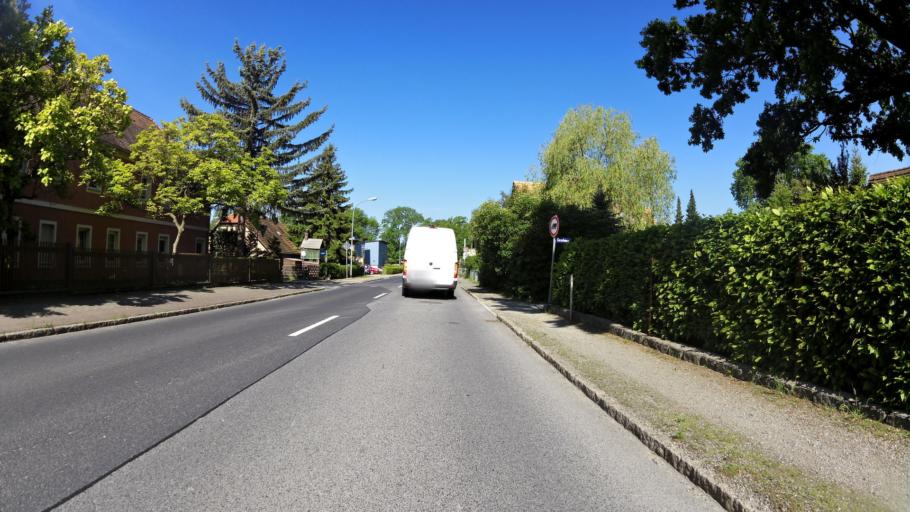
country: DE
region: Saxony
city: Bernsdorf
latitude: 51.3767
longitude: 14.0679
